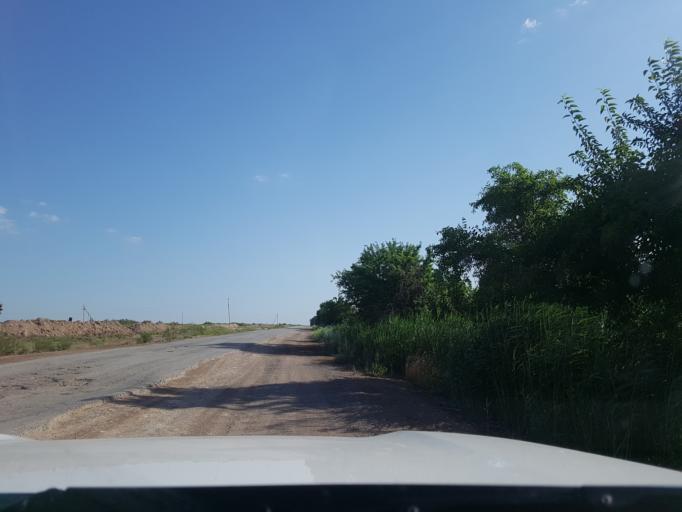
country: TM
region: Dasoguz
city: Koeneuergench
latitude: 41.9314
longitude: 58.7137
